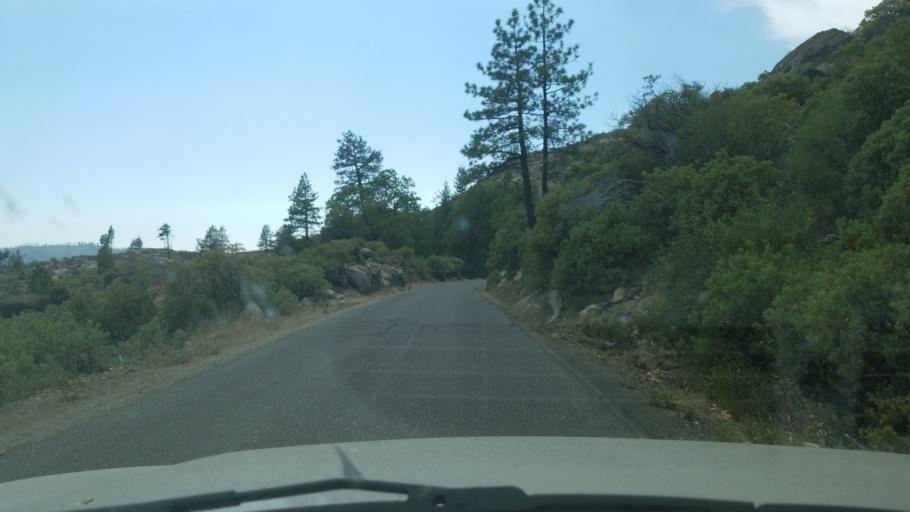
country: US
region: California
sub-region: Mariposa County
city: Yosemite Valley
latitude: 37.9025
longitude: -119.8375
